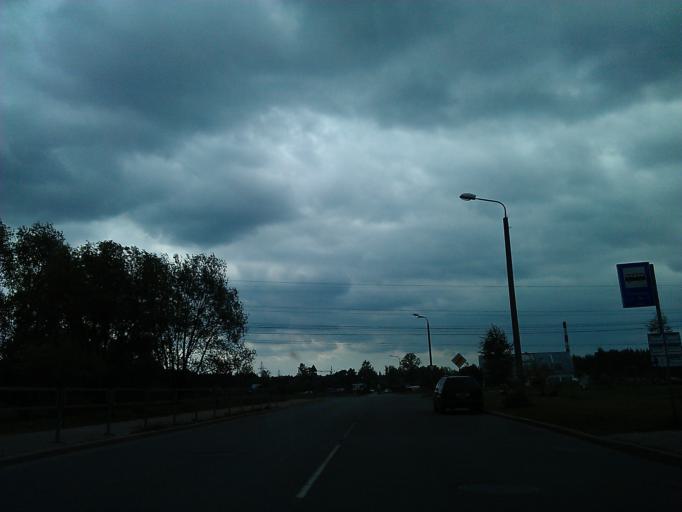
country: LV
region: Kekava
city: Balozi
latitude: 56.8992
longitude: 24.0921
